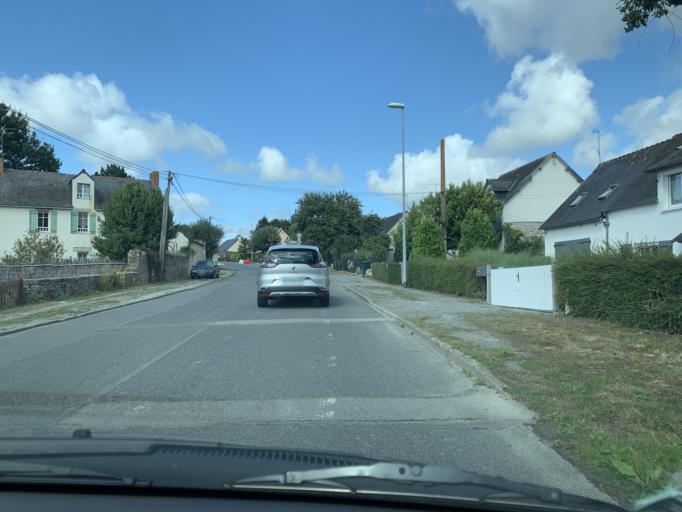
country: FR
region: Pays de la Loire
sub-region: Departement de la Loire-Atlantique
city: Asserac
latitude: 47.4061
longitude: -2.3558
